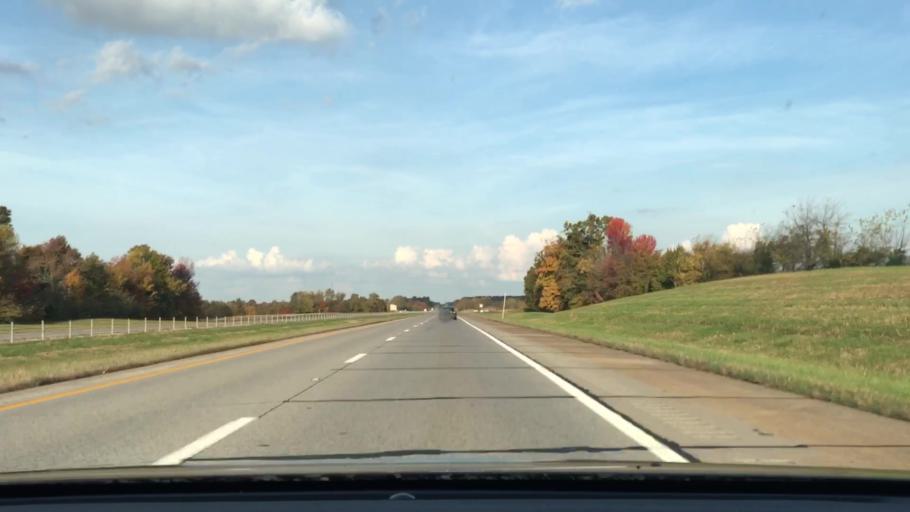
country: US
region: Kentucky
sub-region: Trigg County
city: Cadiz
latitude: 36.9747
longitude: -87.8955
